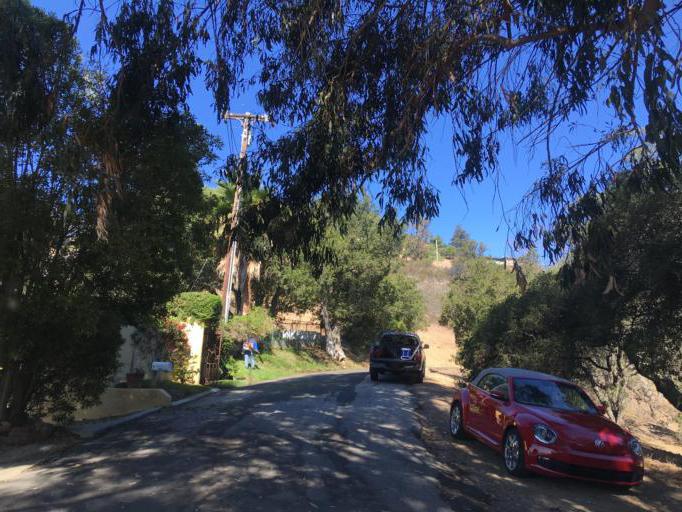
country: US
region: California
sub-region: Los Angeles County
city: Malibu
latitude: 34.0458
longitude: -118.7725
